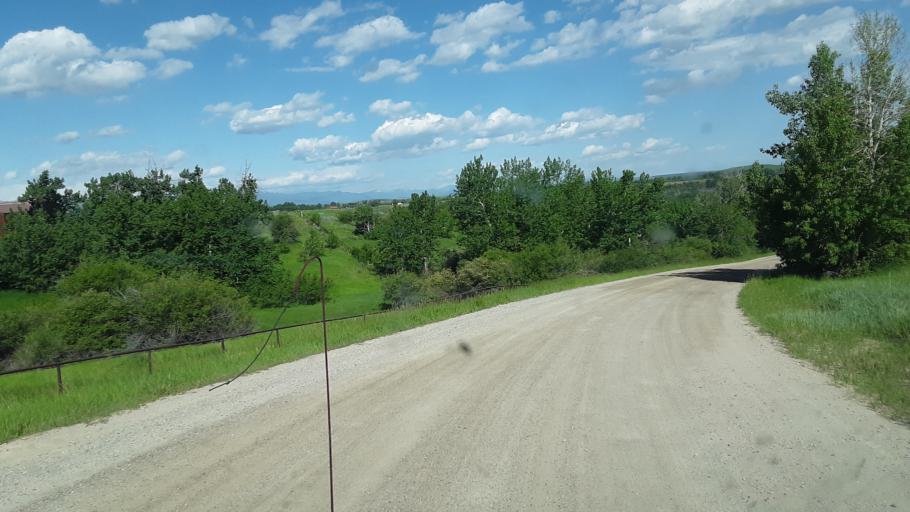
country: US
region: Montana
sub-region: Carbon County
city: Red Lodge
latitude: 45.2780
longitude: -109.2024
